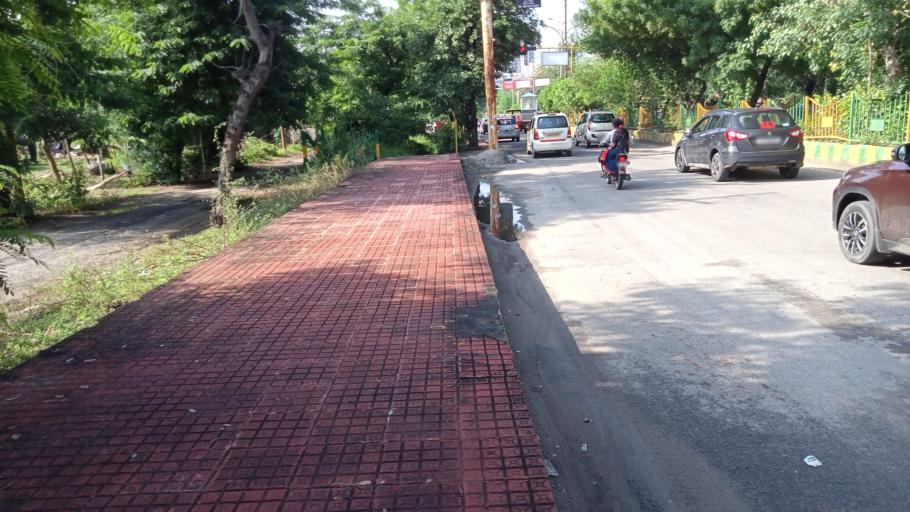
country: IN
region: Uttar Pradesh
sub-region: Ghaziabad
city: Ghaziabad
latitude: 28.6617
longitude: 77.3738
